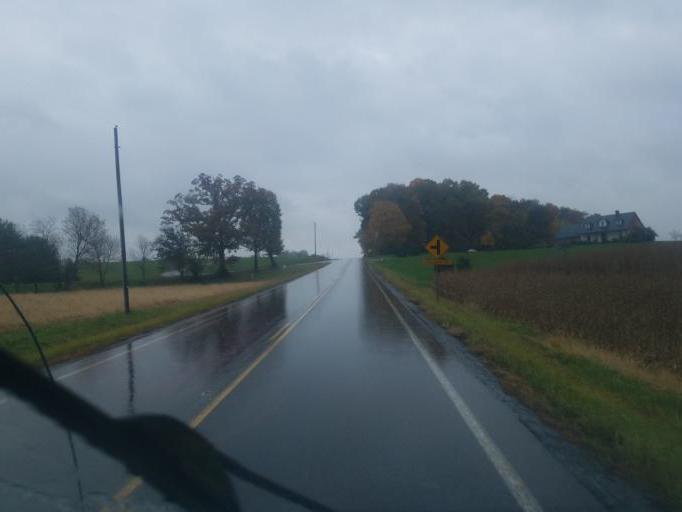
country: US
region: Ohio
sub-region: Licking County
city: Utica
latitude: 40.2495
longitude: -82.3235
